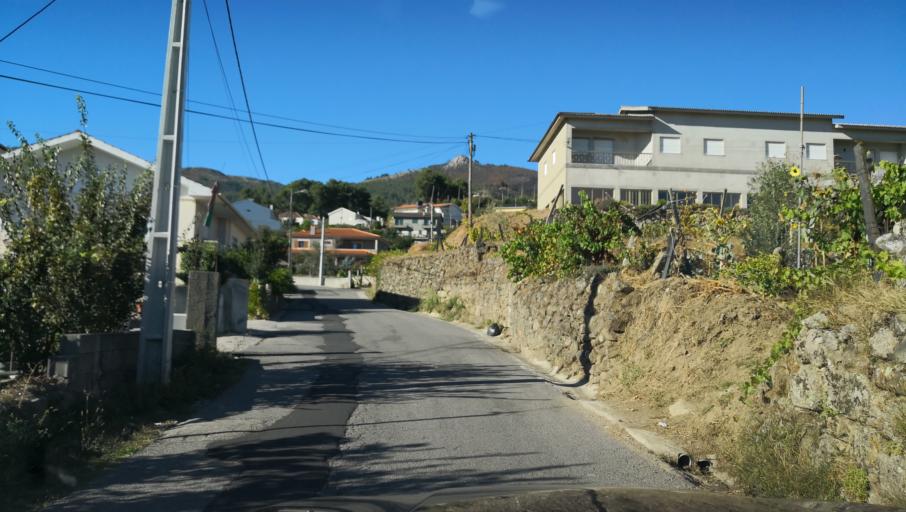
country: PT
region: Vila Real
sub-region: Vila Real
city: Vila Real
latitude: 41.3208
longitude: -7.7680
